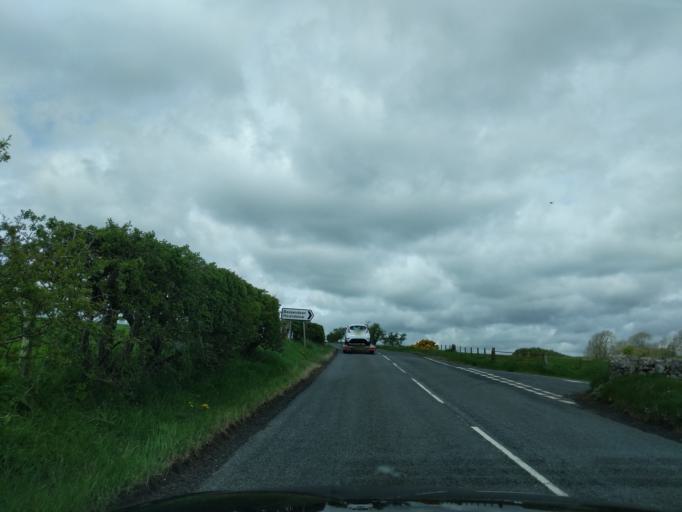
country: GB
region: Scotland
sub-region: The Scottish Borders
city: Earlston
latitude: 55.7008
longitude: -2.6011
